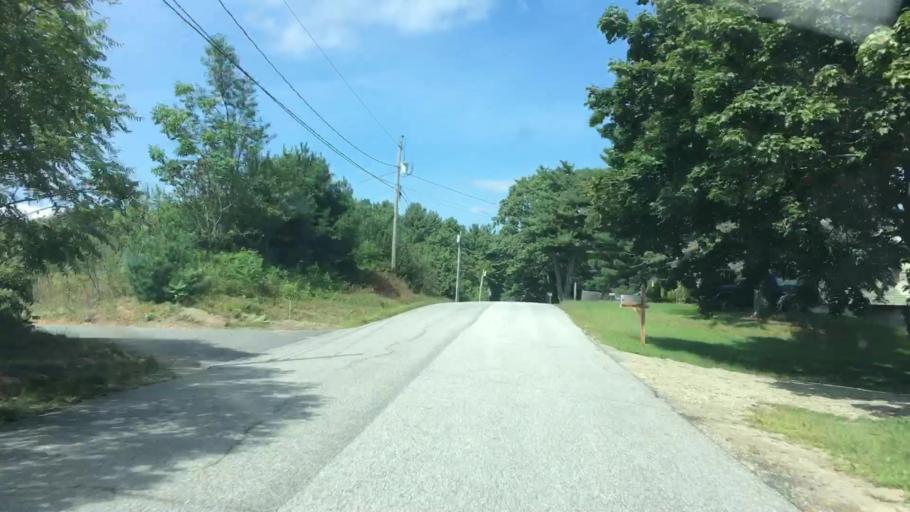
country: US
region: Maine
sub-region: Kennebec County
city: Monmouth
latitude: 44.2725
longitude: -70.0316
